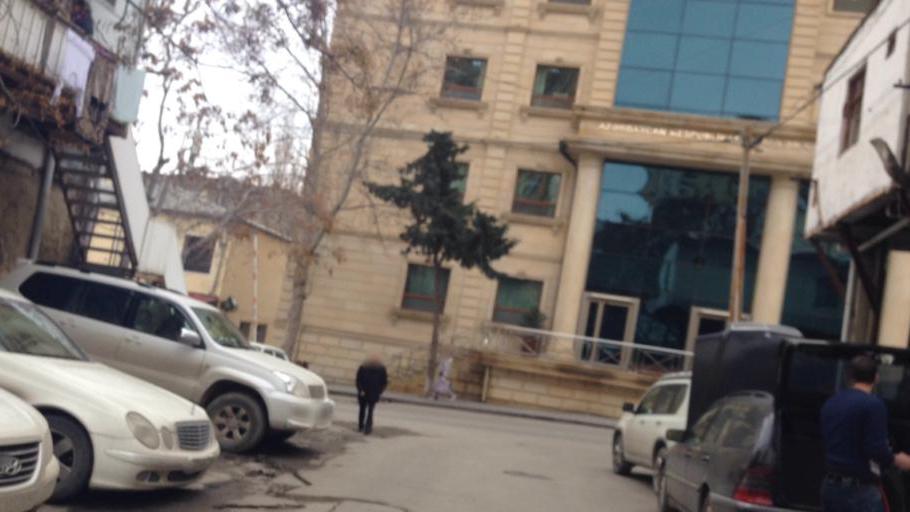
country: AZ
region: Baki
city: Badamdar
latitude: 40.3810
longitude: 49.8255
